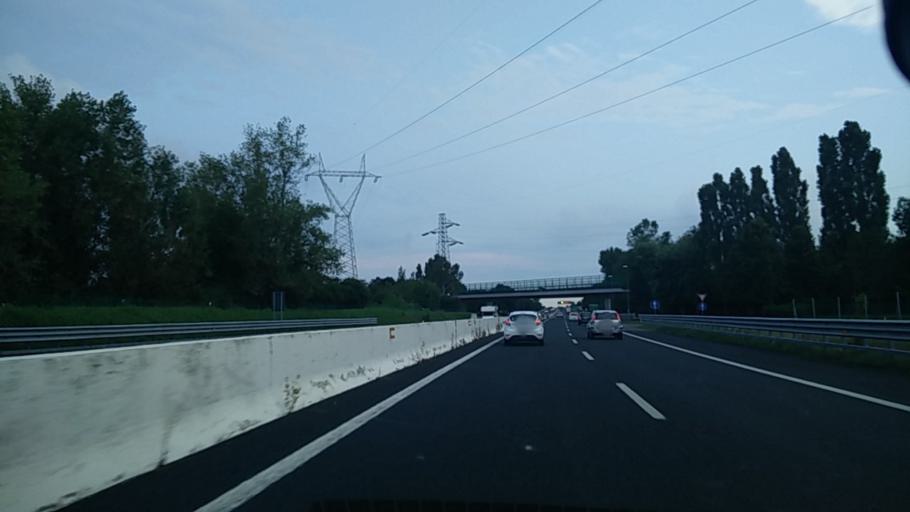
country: IT
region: Friuli Venezia Giulia
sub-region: Provincia di Udine
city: Basaldella
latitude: 46.0407
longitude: 13.2119
